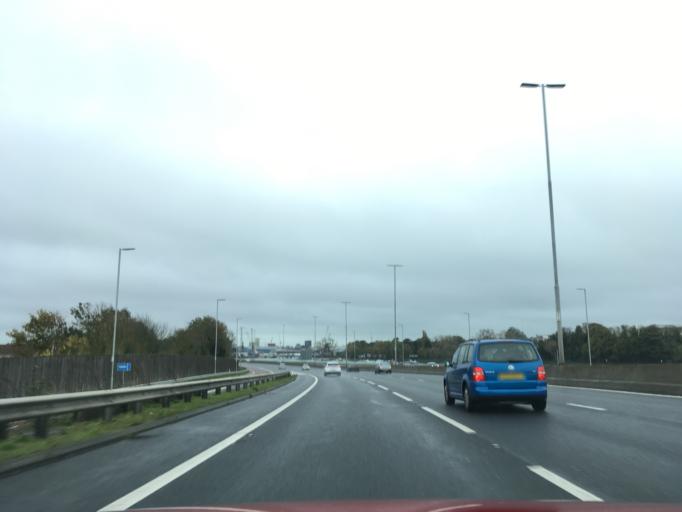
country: GB
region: England
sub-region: Portsmouth
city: Portsmouth
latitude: 50.8231
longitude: -1.0926
